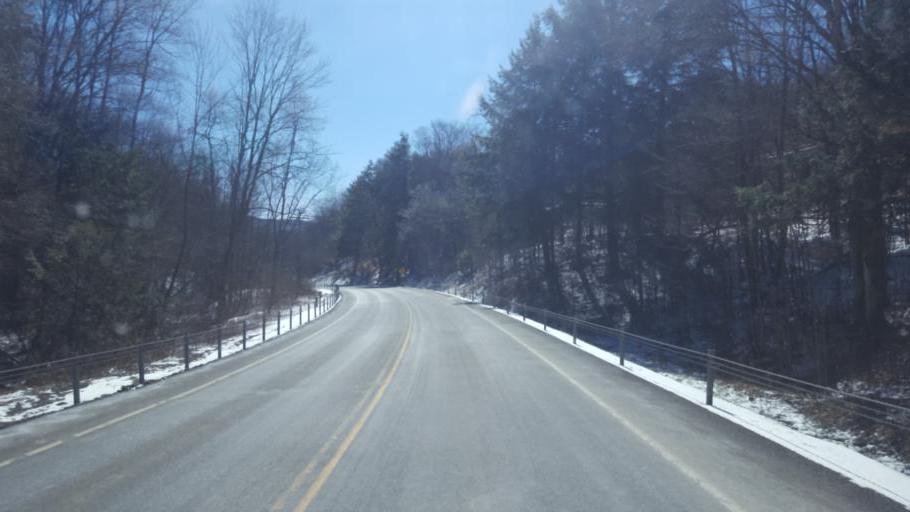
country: US
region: New York
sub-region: Allegany County
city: Andover
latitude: 42.0519
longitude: -77.7933
